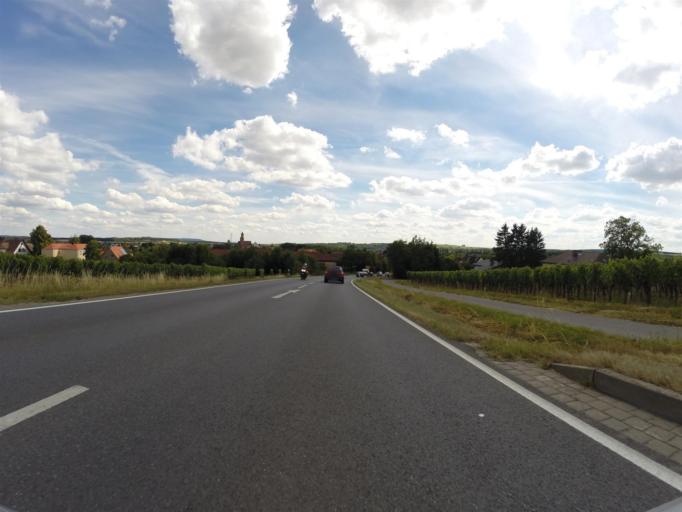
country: DE
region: Bavaria
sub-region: Regierungsbezirk Unterfranken
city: Volkach
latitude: 49.8729
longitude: 10.2257
